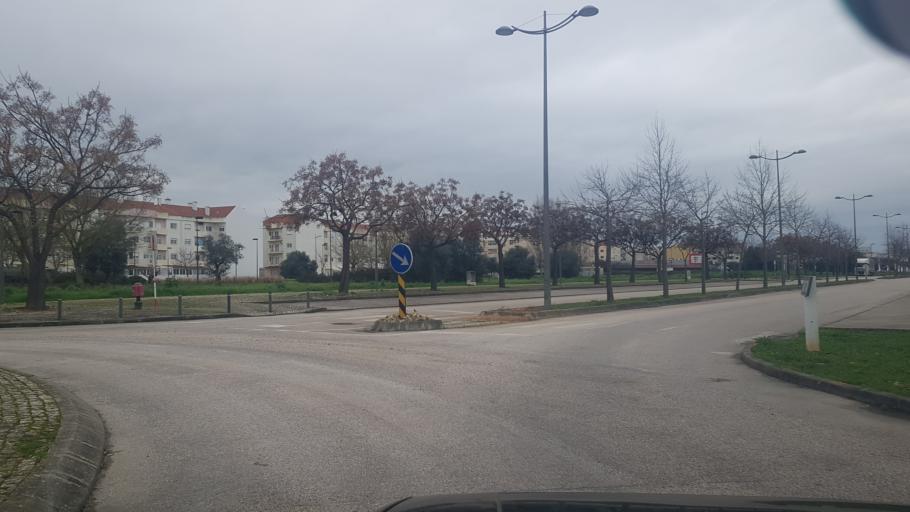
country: PT
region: Santarem
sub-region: Entroncamento
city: Entroncamento
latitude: 39.4568
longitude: -8.4646
